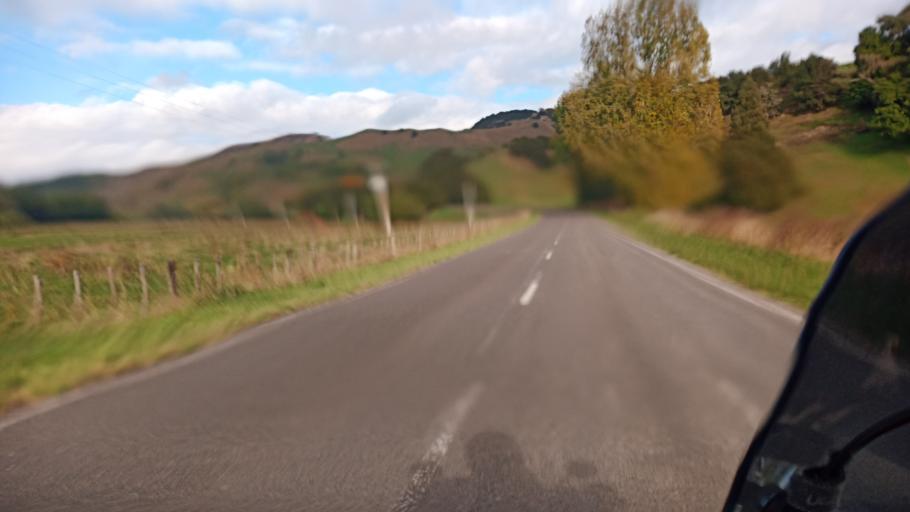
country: NZ
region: Gisborne
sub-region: Gisborne District
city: Gisborne
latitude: -38.5902
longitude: 177.7814
